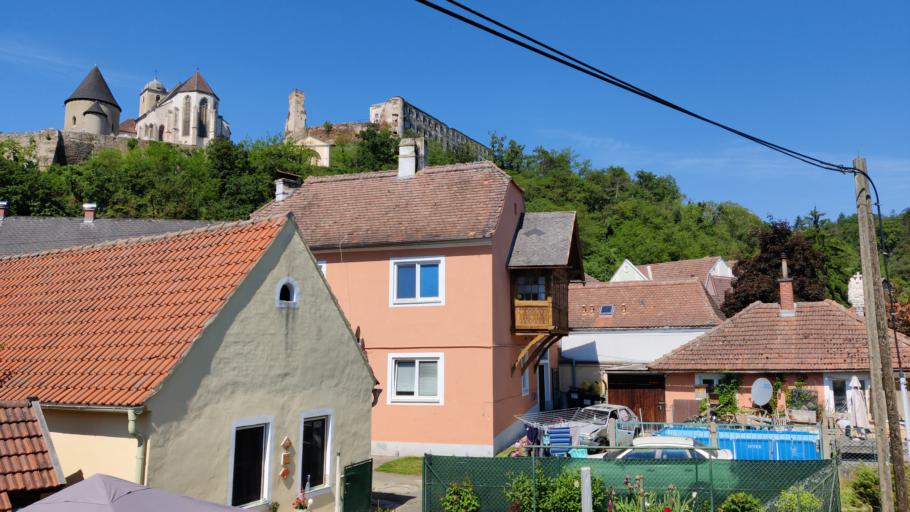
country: AT
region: Lower Austria
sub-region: Politischer Bezirk Horn
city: Gars am Kamp
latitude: 48.5941
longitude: 15.6570
